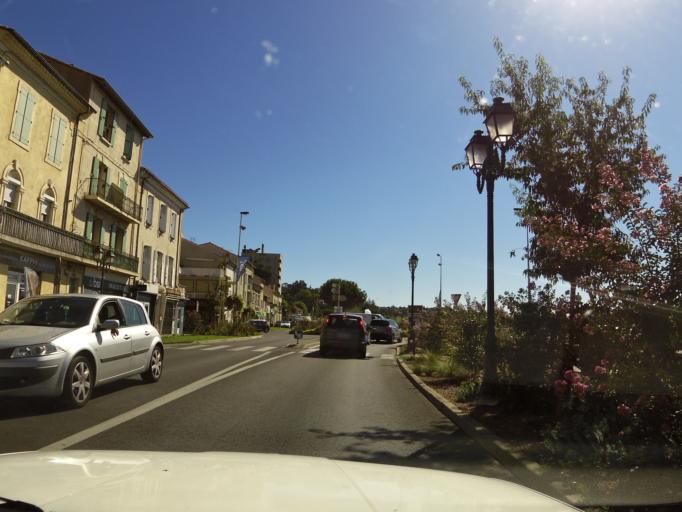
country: FR
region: Languedoc-Roussillon
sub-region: Departement du Gard
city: Ales
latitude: 44.1213
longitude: 4.0841
